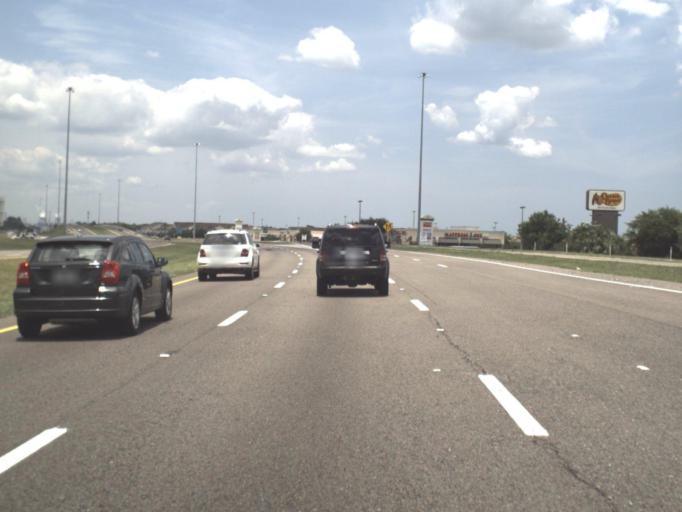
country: US
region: Florida
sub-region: Duval County
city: Jacksonville
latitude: 30.3316
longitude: -81.5526
